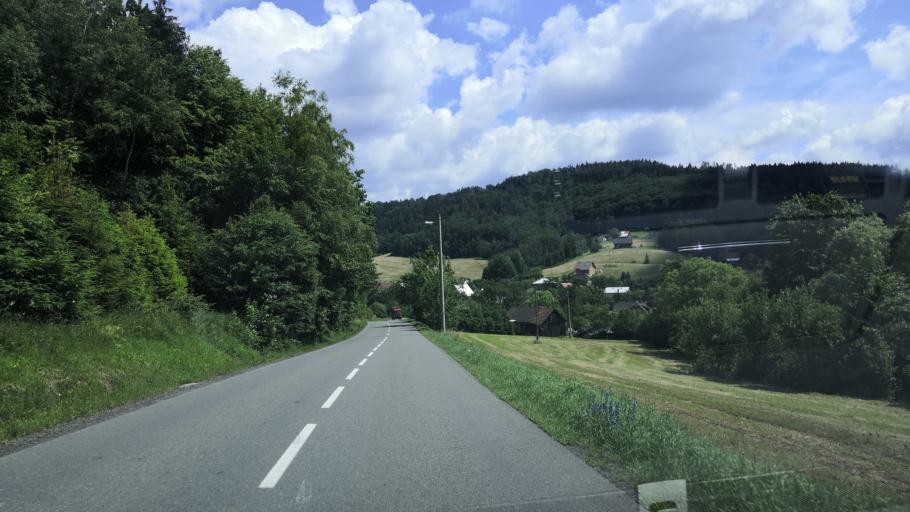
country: CZ
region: Zlin
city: Valasska Bystrice
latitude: 49.4260
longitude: 18.1166
